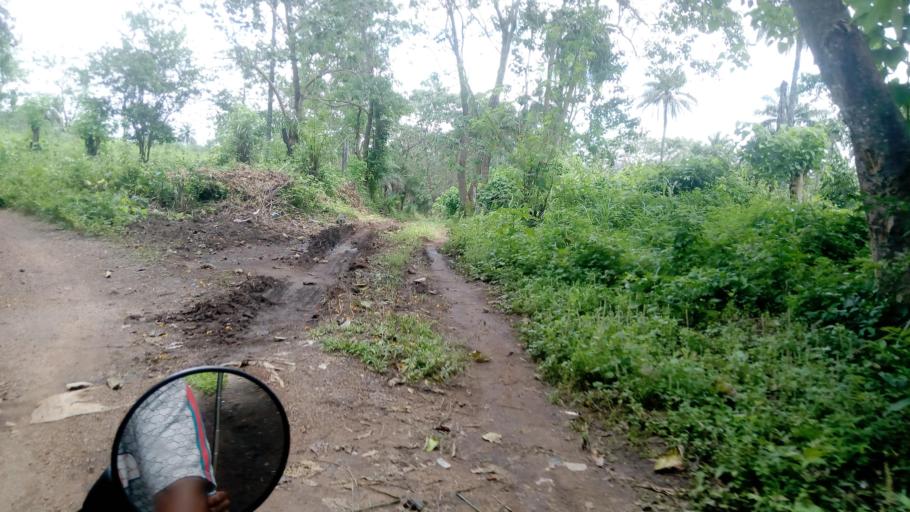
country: SL
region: Northern Province
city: Binkolo
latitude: 8.9276
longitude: -12.0087
